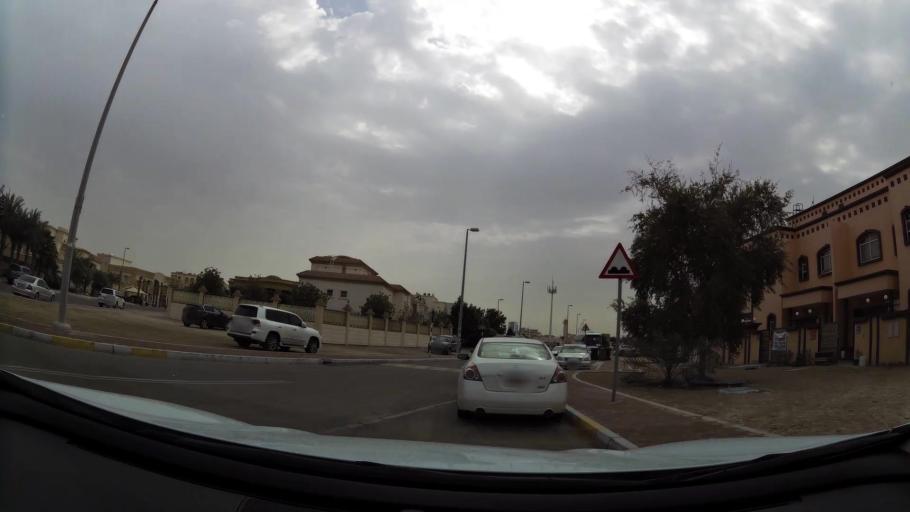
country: AE
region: Abu Dhabi
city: Abu Dhabi
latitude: 24.4317
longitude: 54.4428
